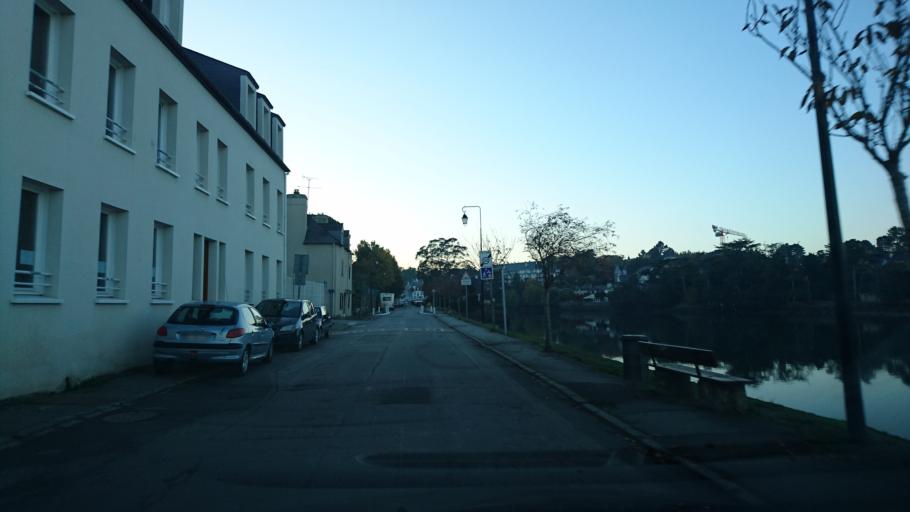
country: FR
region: Brittany
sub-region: Departement du Morbihan
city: Pluneret
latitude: 47.6663
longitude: -2.9738
